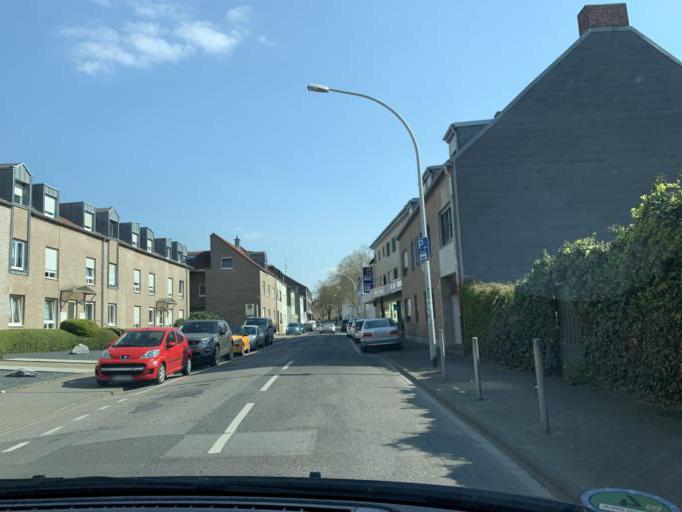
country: DE
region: North Rhine-Westphalia
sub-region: Regierungsbezirk Dusseldorf
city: Monchengladbach
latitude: 51.1331
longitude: 6.4553
